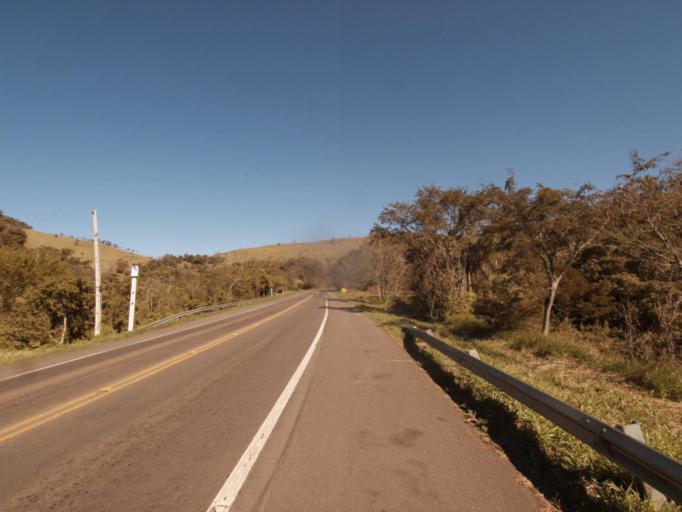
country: BR
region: Rio Grande do Sul
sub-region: Frederico Westphalen
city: Frederico Westphalen
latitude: -26.8236
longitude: -53.4122
